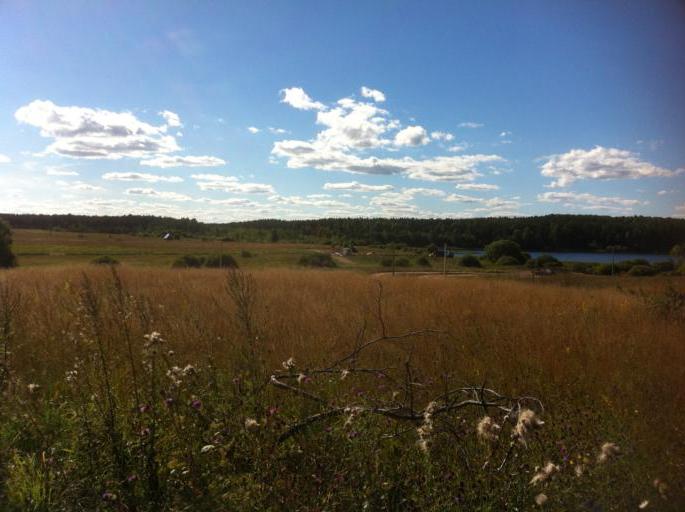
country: RU
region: Pskov
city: Izborsk
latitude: 57.8226
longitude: 27.9663
